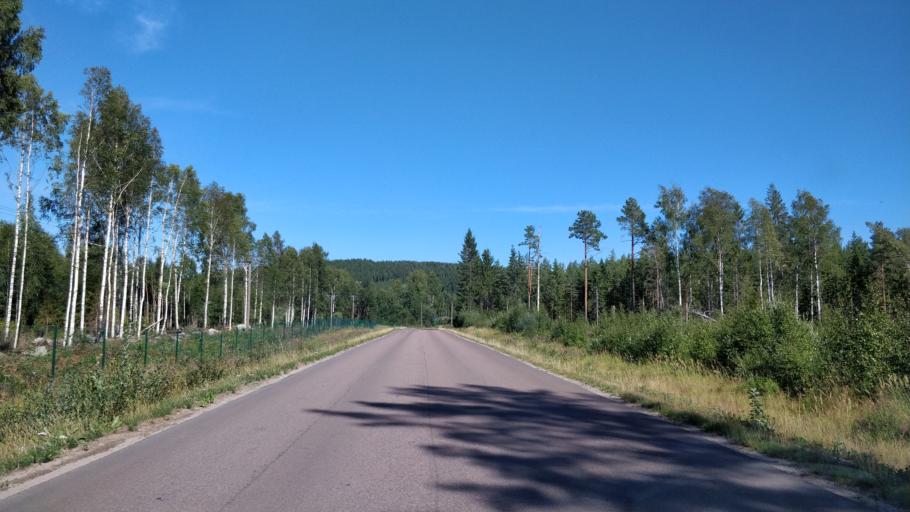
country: SE
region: Vaermland
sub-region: Hagfors Kommun
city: Hagfors
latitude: 60.0383
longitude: 13.7322
